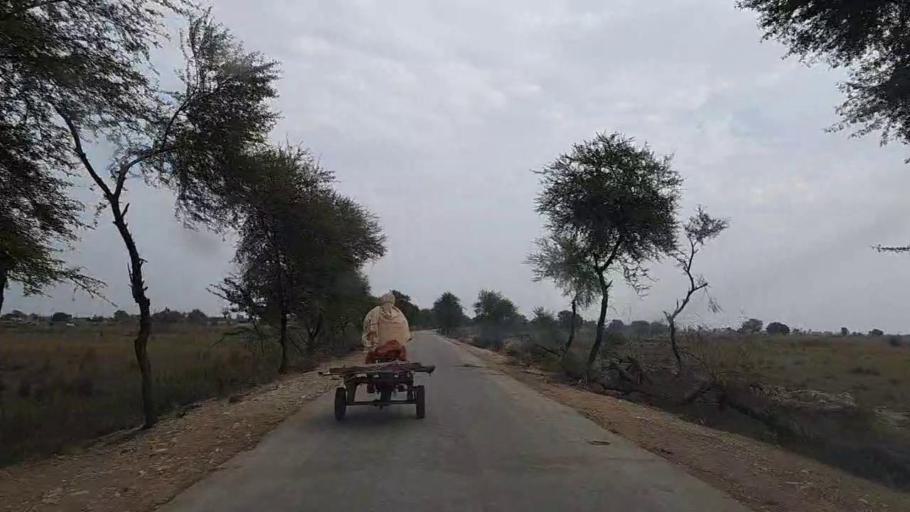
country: PK
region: Sindh
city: Sanghar
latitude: 26.2286
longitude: 69.0081
